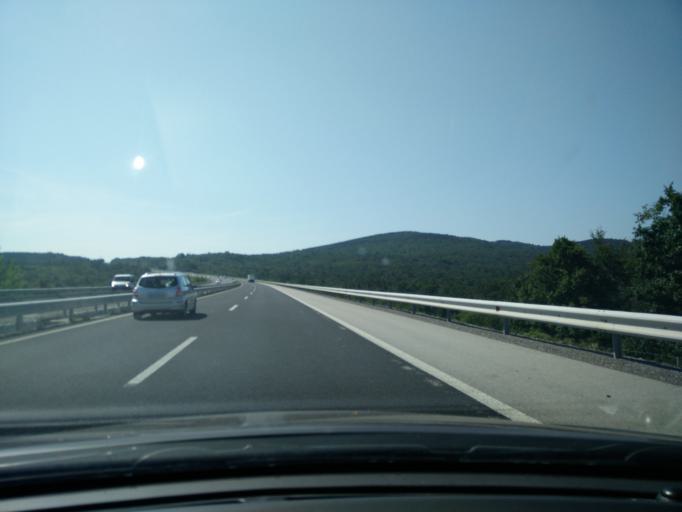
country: SI
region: Divaca
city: Divaca
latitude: 45.6538
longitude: 13.9612
